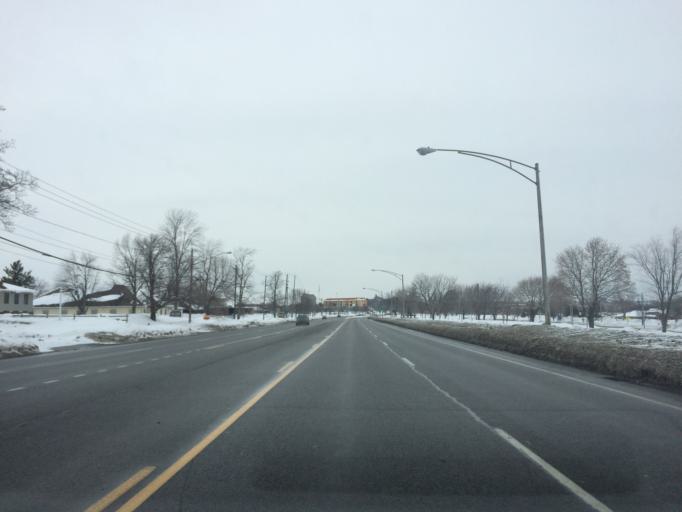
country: US
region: New York
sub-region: Monroe County
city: Rochester
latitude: 43.1008
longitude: -77.6144
